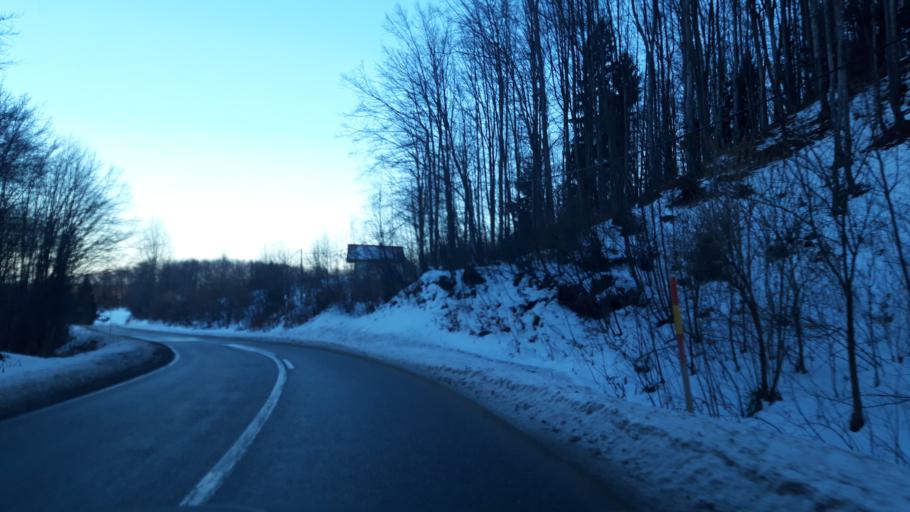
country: BA
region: Republika Srpska
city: Vlasenica
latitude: 44.1602
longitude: 18.9393
